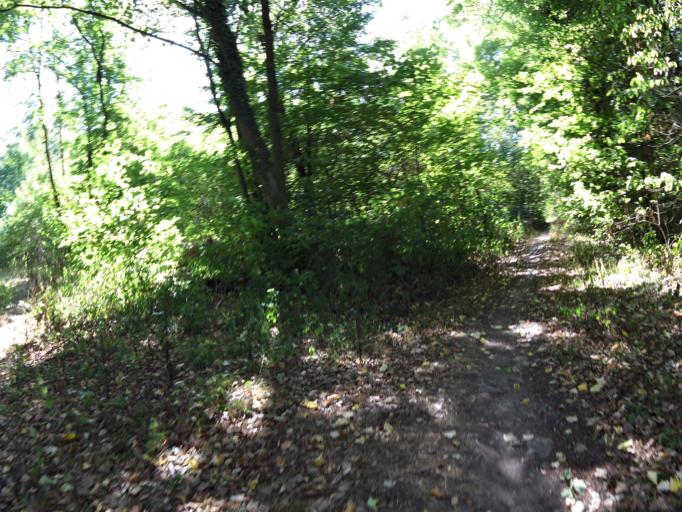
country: DE
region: Bavaria
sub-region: Regierungsbezirk Unterfranken
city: Waldbuttelbrunn
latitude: 49.7683
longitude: 9.8551
